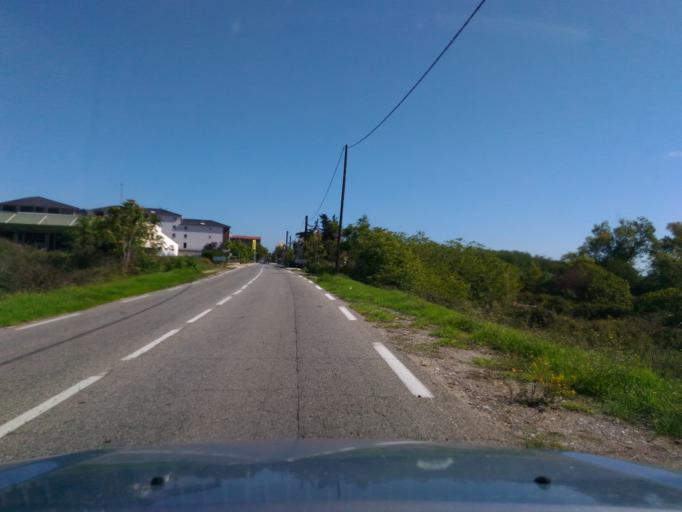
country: FR
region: Corsica
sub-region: Departement de la Haute-Corse
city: Aleria
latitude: 42.1126
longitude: 9.5095
